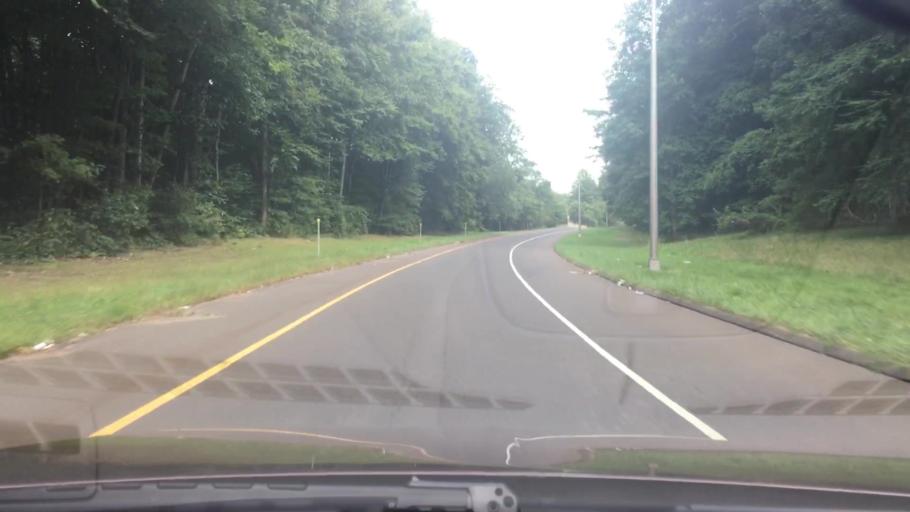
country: US
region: Connecticut
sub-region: Fairfield County
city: Trumbull
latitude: 41.2344
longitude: -73.1937
